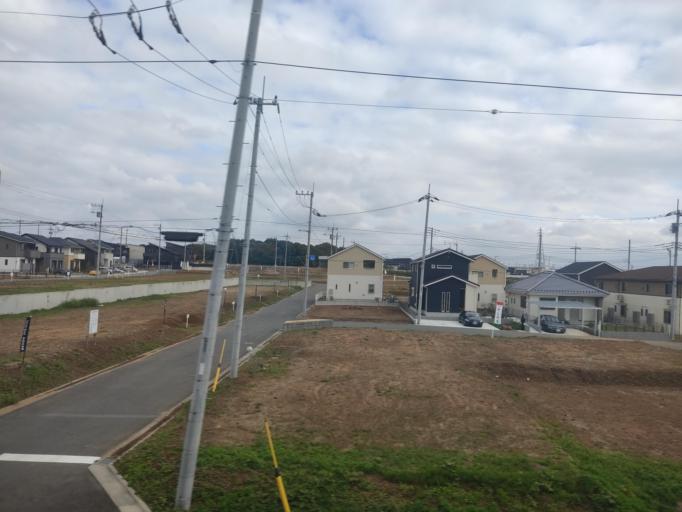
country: JP
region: Ibaraki
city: Mitsukaido
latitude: 36.0386
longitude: 140.0584
